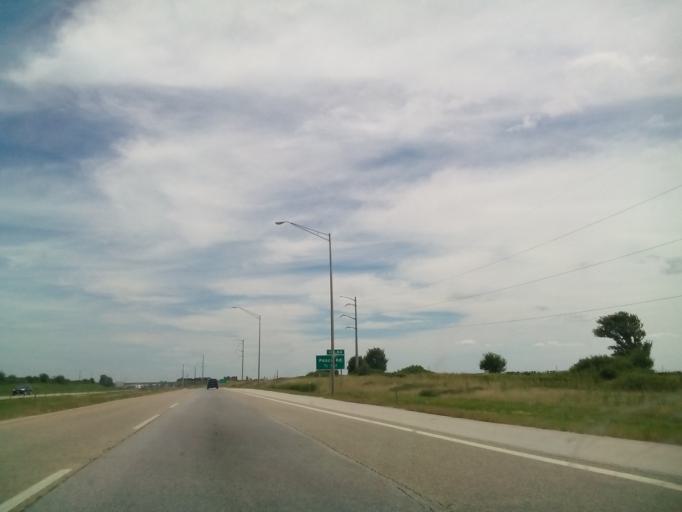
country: US
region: Illinois
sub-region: DeKalb County
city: DeKalb
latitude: 41.9007
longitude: -88.7328
